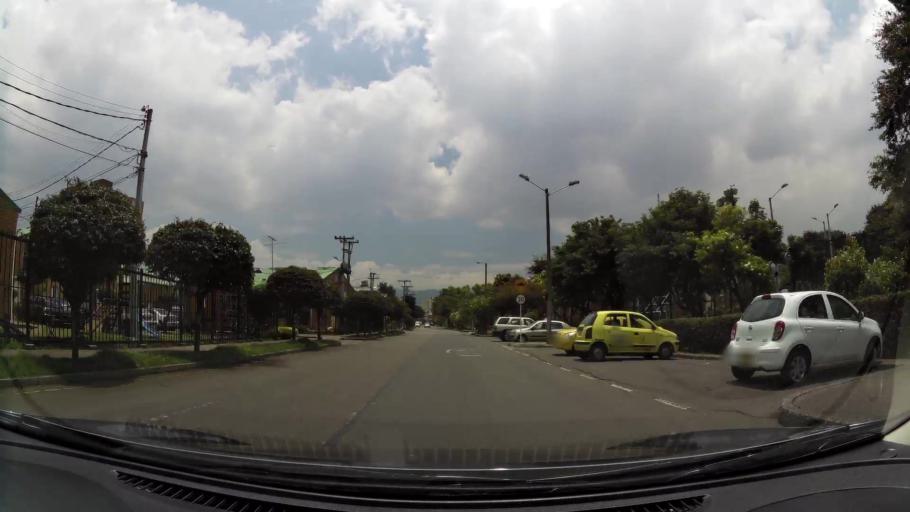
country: CO
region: Cundinamarca
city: Cota
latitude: 4.7523
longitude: -74.0631
